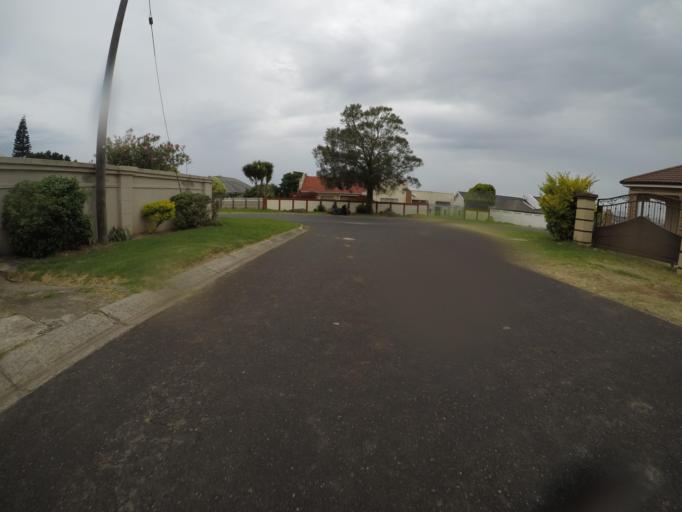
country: ZA
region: Eastern Cape
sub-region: Buffalo City Metropolitan Municipality
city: East London
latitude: -32.9891
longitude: 27.8467
